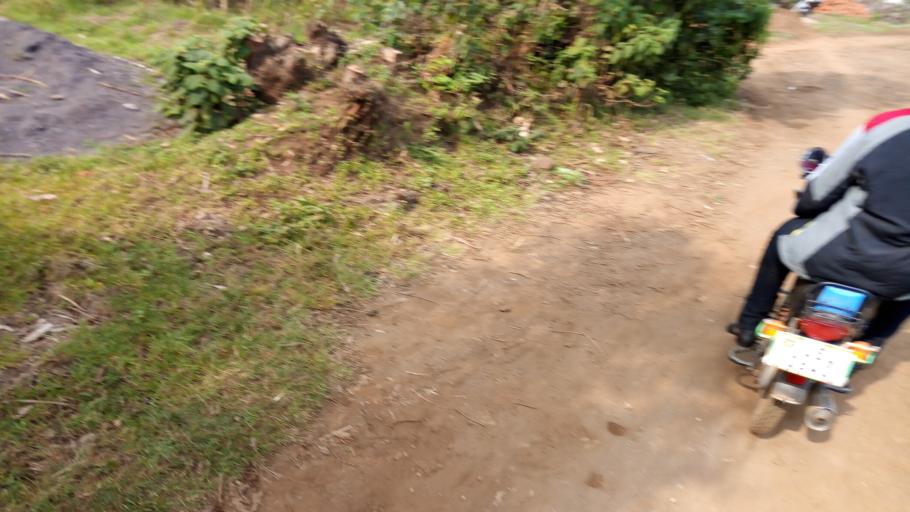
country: UG
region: Western Region
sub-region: Kisoro District
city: Kisoro
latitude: -1.3095
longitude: 29.6581
